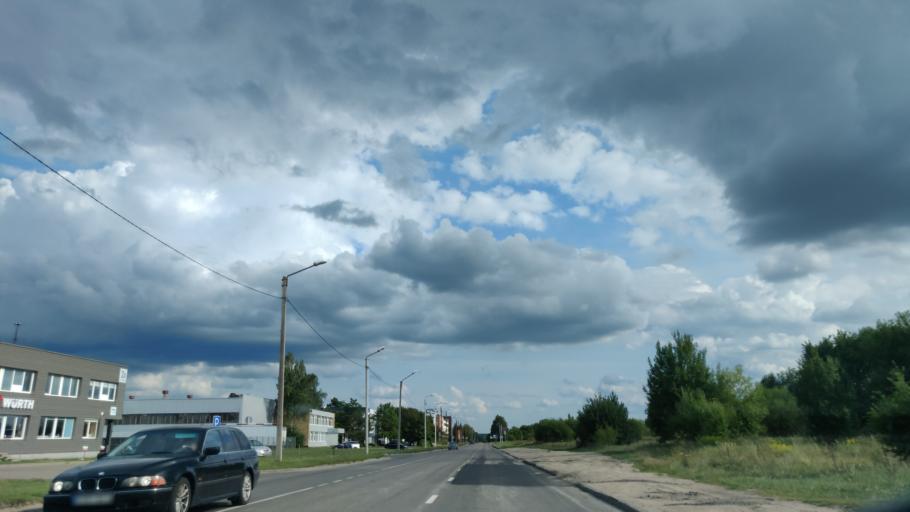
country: LT
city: Baltoji Voke
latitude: 54.6283
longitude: 25.1379
